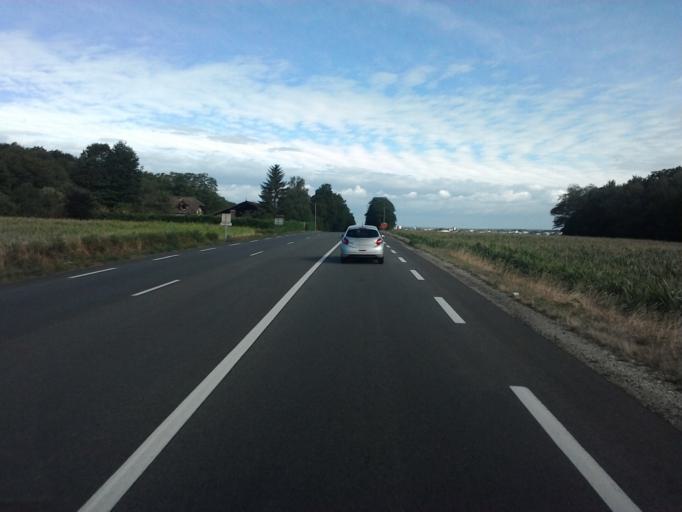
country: FR
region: Rhone-Alpes
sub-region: Departement de l'Ain
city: Bourg-en-Bresse
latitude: 46.1805
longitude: 5.2525
